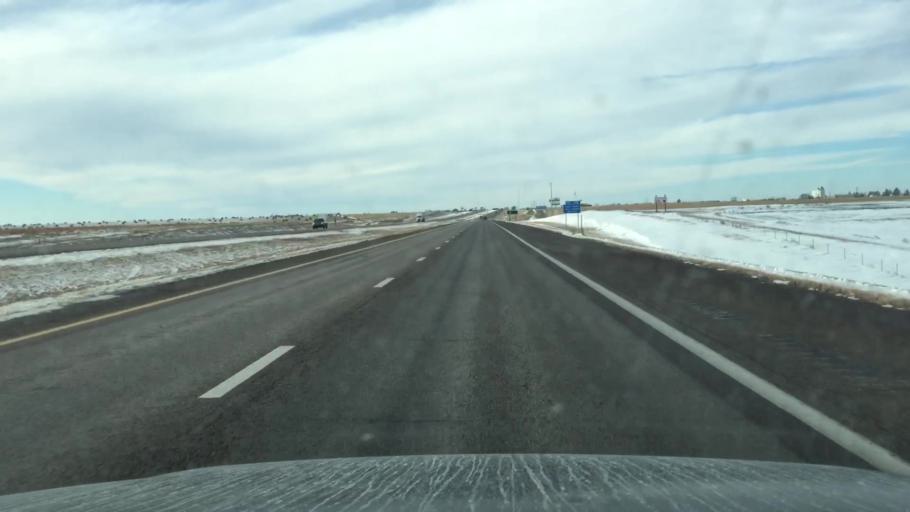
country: US
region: Kansas
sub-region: Trego County
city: WaKeeney
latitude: 39.0079
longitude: -99.8549
